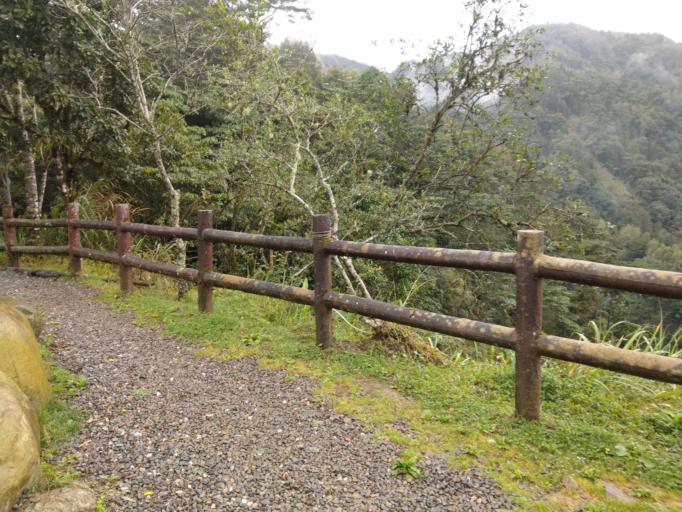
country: TW
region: Taiwan
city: Lugu
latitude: 23.6395
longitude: 120.7863
